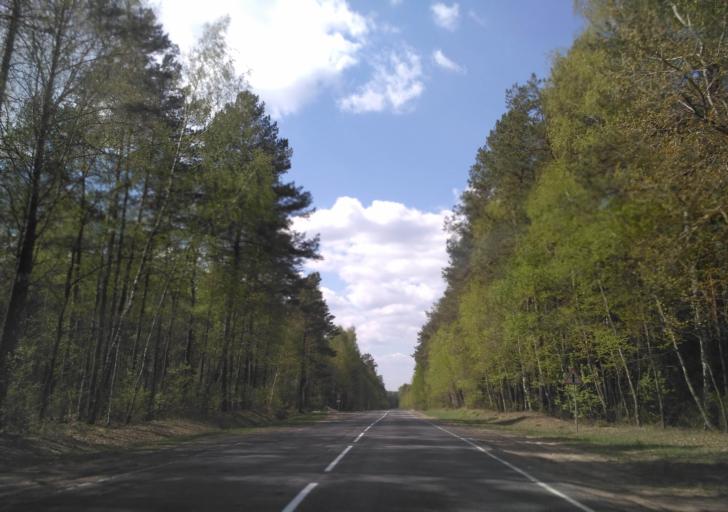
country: BY
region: Minsk
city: Vilyeyka
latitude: 54.4989
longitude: 27.1086
